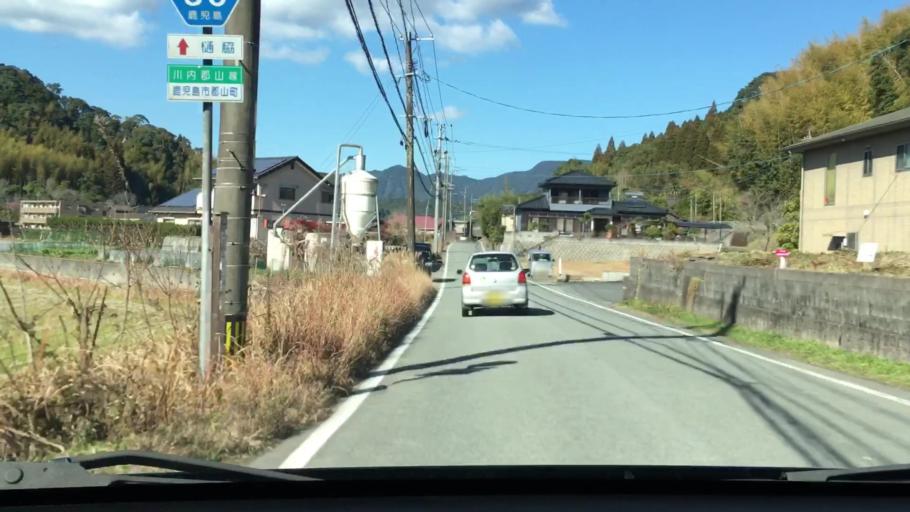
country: JP
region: Kagoshima
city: Ijuin
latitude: 31.6840
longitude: 130.4694
